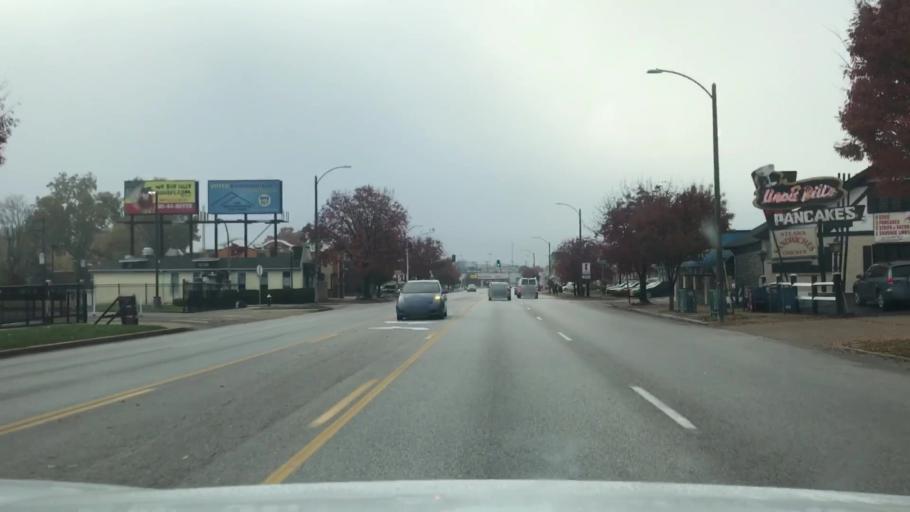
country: US
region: Missouri
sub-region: Saint Louis County
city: Maplewood
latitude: 38.5972
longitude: -90.2708
